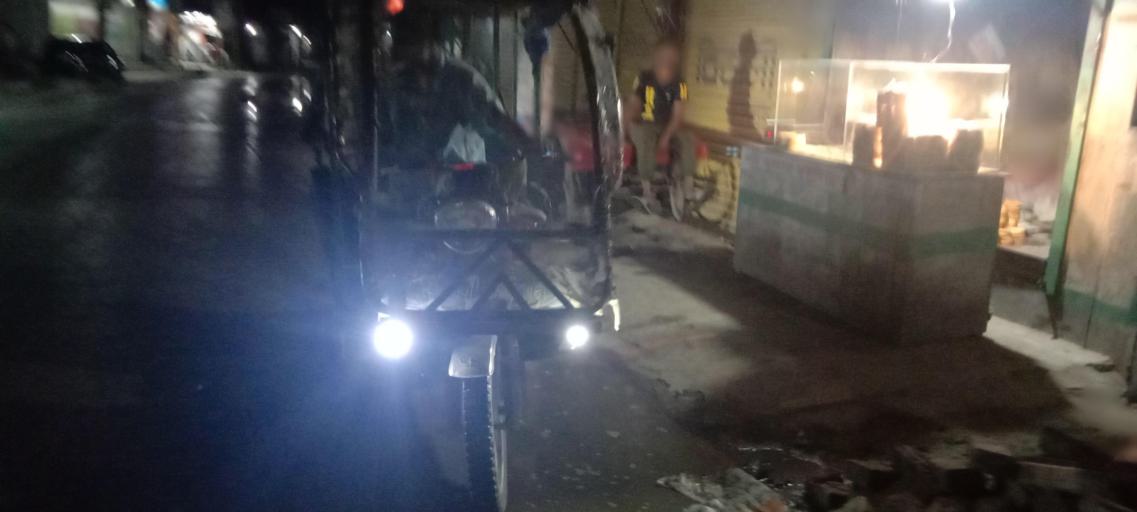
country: BD
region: Dhaka
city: Azimpur
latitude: 23.6914
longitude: 90.3095
